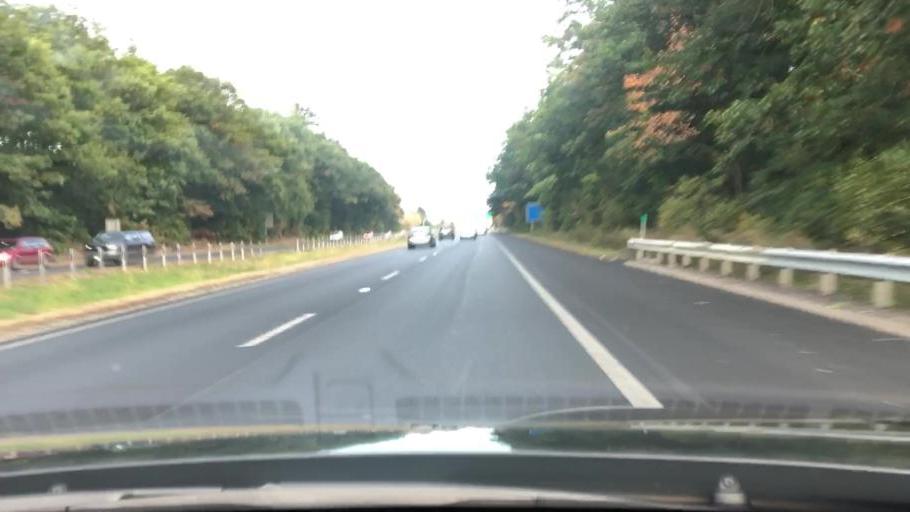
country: US
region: Massachusetts
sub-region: Essex County
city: Methuen
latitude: 42.7380
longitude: -71.1782
